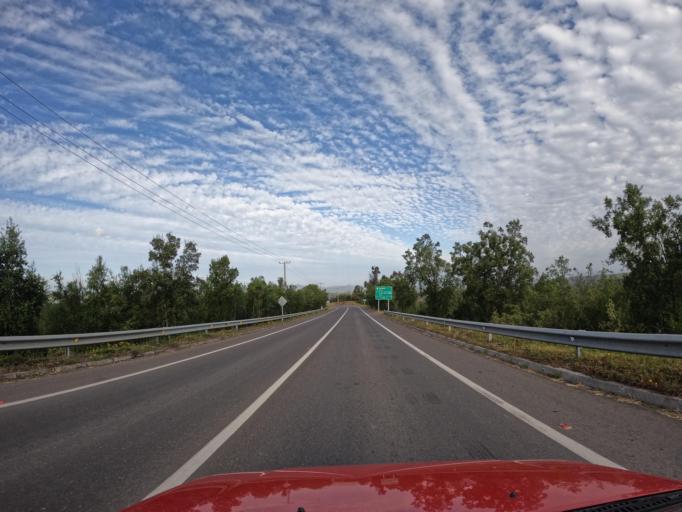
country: CL
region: Valparaiso
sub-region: San Antonio Province
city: San Antonio
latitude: -34.0508
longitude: -71.6035
